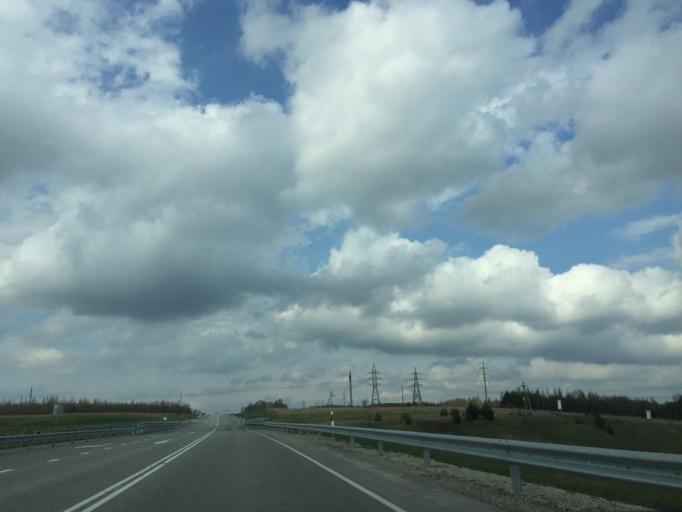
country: EE
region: Tartu
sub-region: Elva linn
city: Elva
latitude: 58.2417
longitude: 26.4079
